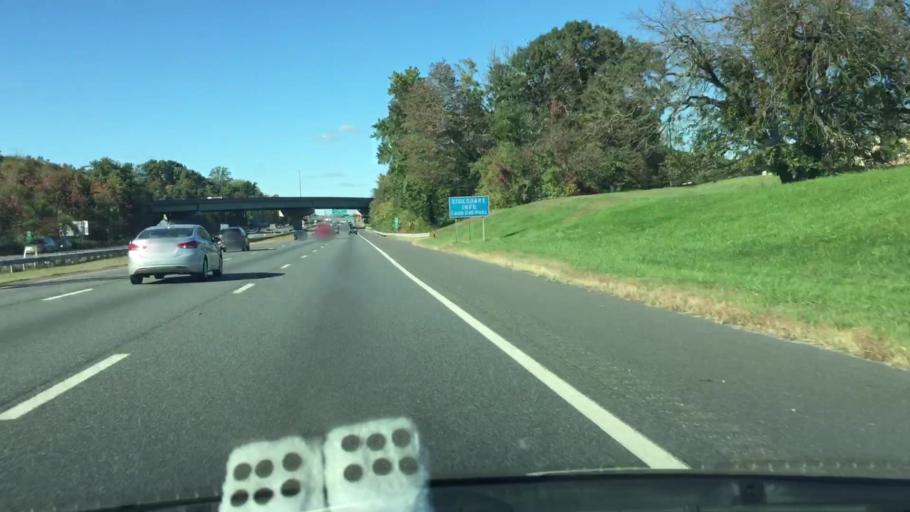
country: US
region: New Jersey
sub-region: Camden County
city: Glendora
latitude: 39.8422
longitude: -75.0934
